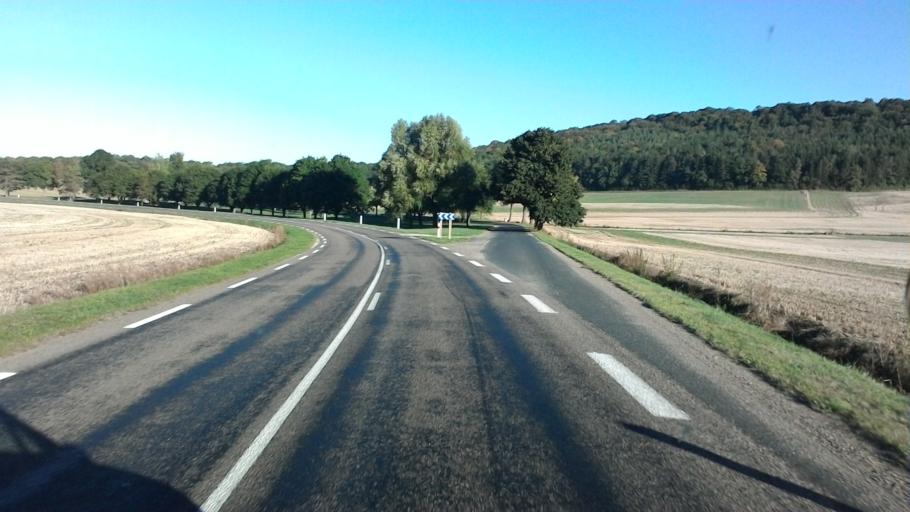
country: FR
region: Champagne-Ardenne
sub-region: Departement de la Haute-Marne
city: Doulaincourt-Saucourt
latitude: 48.2607
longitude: 5.3559
